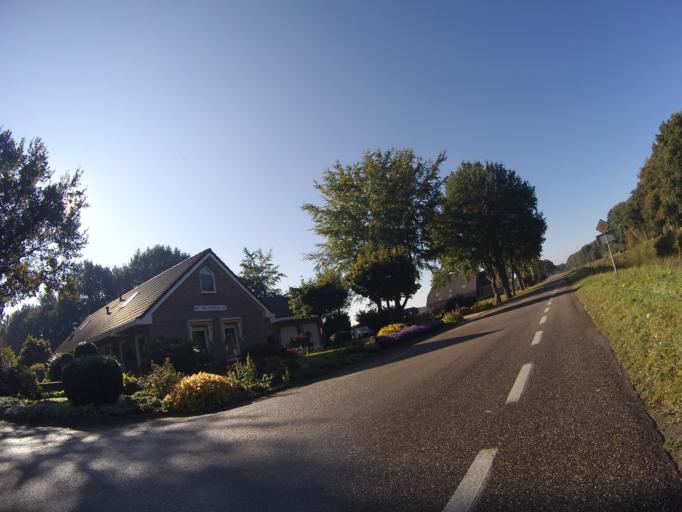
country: NL
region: Drenthe
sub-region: Gemeente Coevorden
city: Dalen
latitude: 52.7322
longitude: 6.7079
